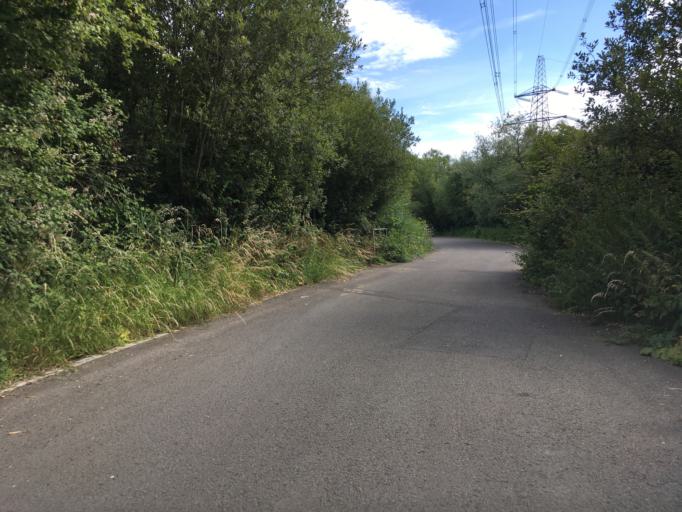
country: GB
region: Wales
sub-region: Newport
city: Nash
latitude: 51.5690
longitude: -2.9598
